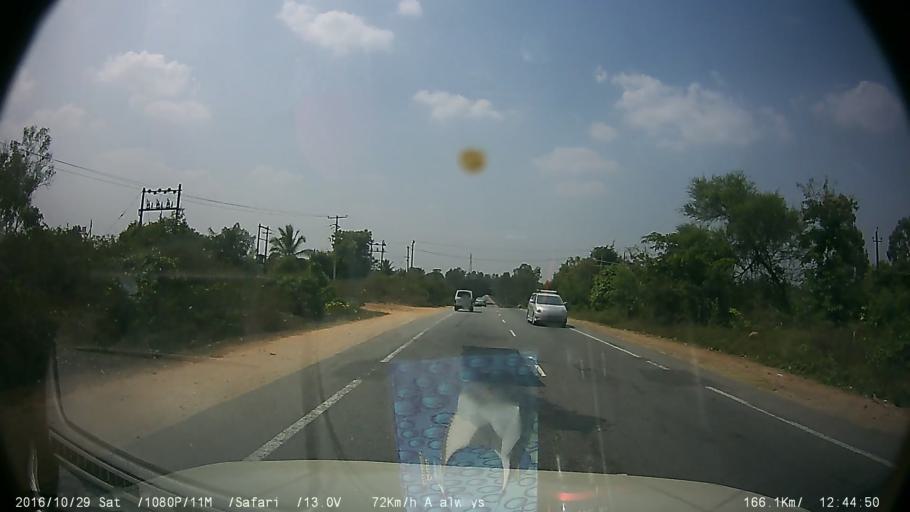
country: IN
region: Karnataka
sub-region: Mysore
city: Hunsur
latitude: 12.3423
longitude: 76.4069
